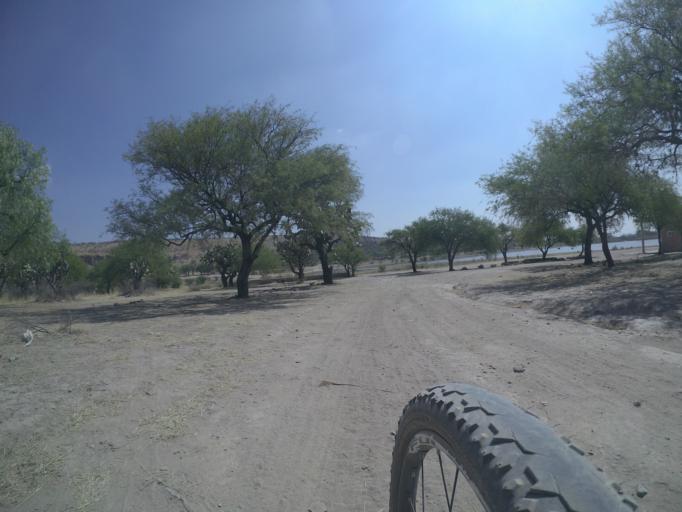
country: MX
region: Aguascalientes
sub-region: Jesus Maria
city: Paseos de las Haciendas [Fraccionamiento]
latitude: 21.9992
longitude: -102.3666
